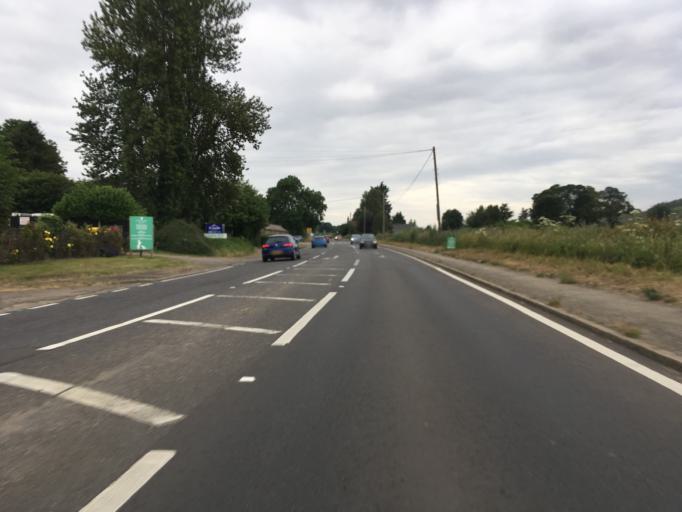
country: GB
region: England
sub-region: Central Bedfordshire
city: Kensworth
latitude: 51.8645
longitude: -0.4861
